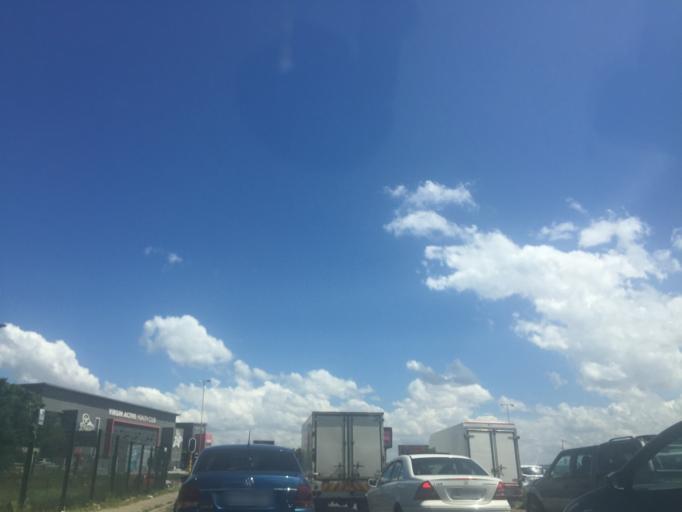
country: ZA
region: Gauteng
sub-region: City of Johannesburg Metropolitan Municipality
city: Diepsloot
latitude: -26.0560
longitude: 28.0224
